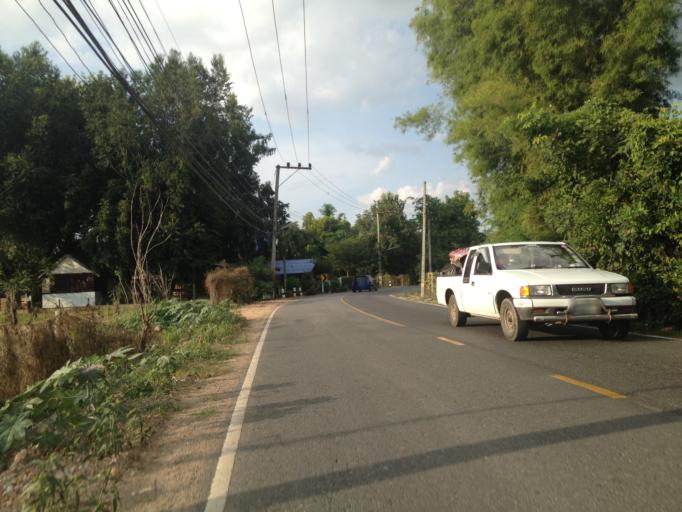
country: TH
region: Chiang Mai
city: Saraphi
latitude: 18.6956
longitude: 98.9851
